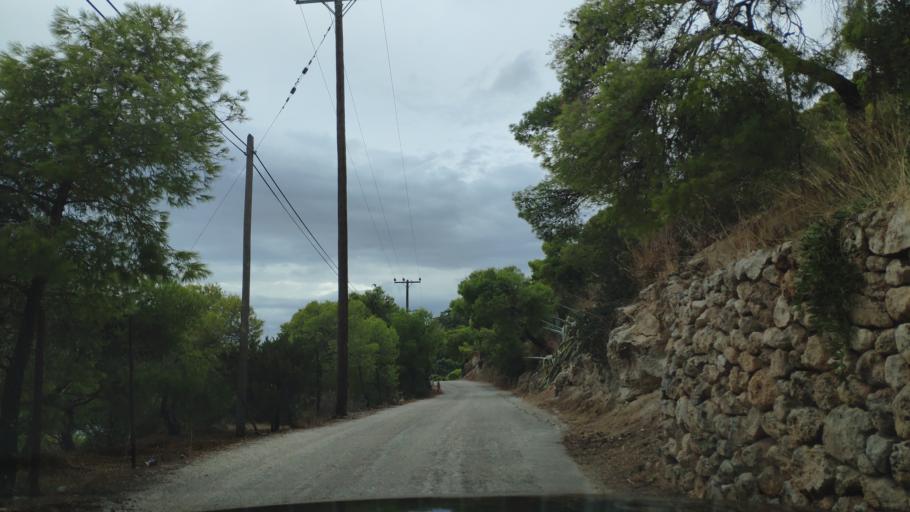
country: GR
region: Peloponnese
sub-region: Nomos Korinthias
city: Perachora
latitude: 38.0305
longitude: 22.8726
